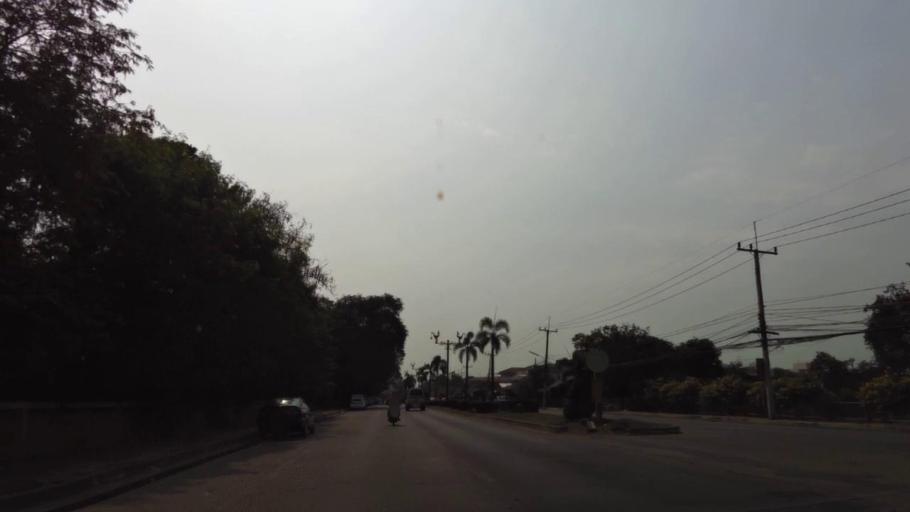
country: TH
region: Phra Nakhon Si Ayutthaya
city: Phra Nakhon Si Ayutthaya
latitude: 14.3501
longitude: 100.5696
